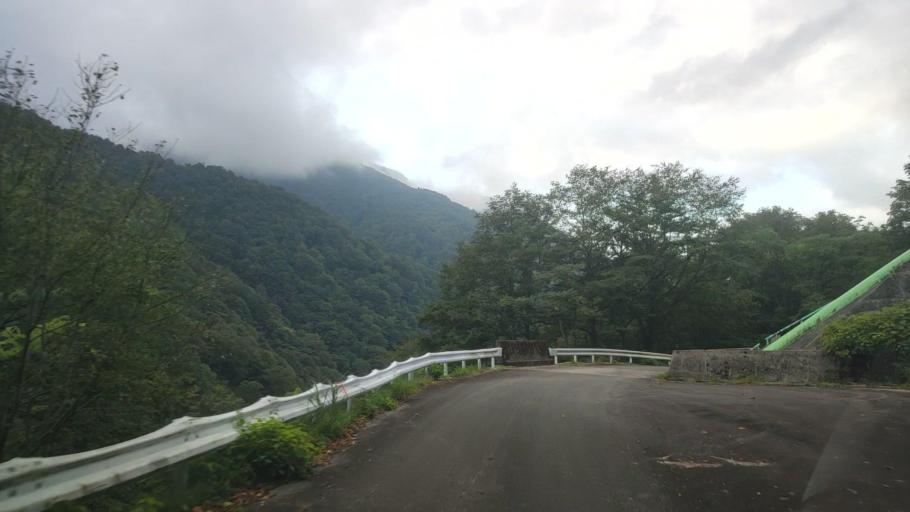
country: JP
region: Toyama
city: Yatsuomachi-higashikumisaka
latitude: 36.3987
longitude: 137.0740
